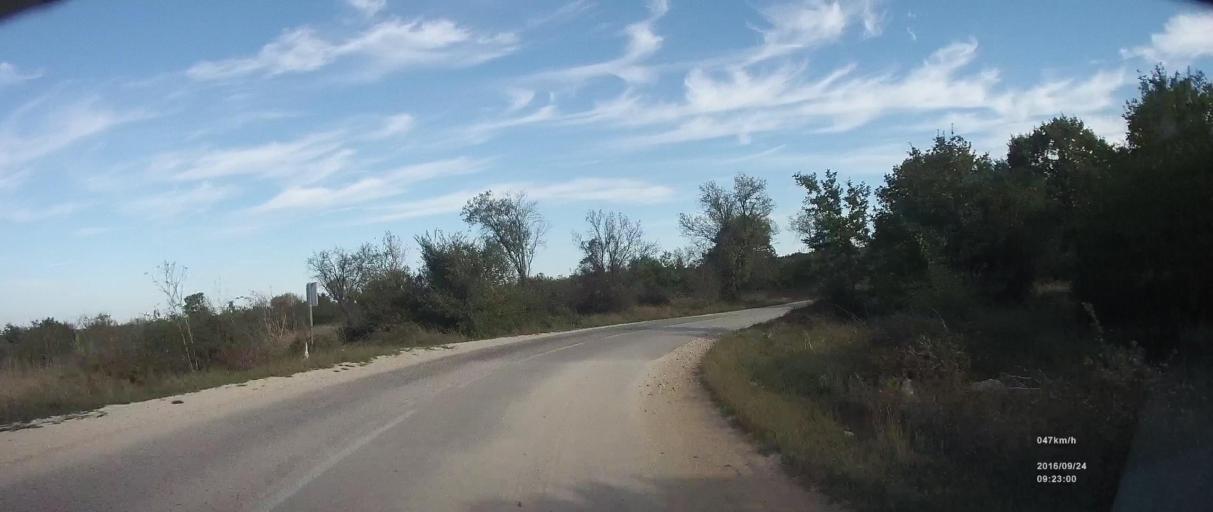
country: HR
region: Zadarska
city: Polaca
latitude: 44.0714
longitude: 15.4748
